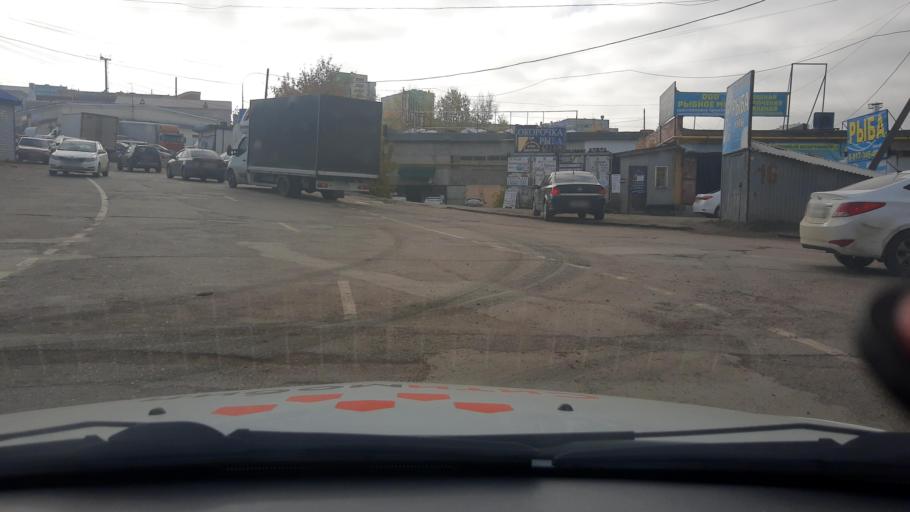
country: RU
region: Bashkortostan
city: Ufa
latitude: 54.7147
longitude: 55.9865
